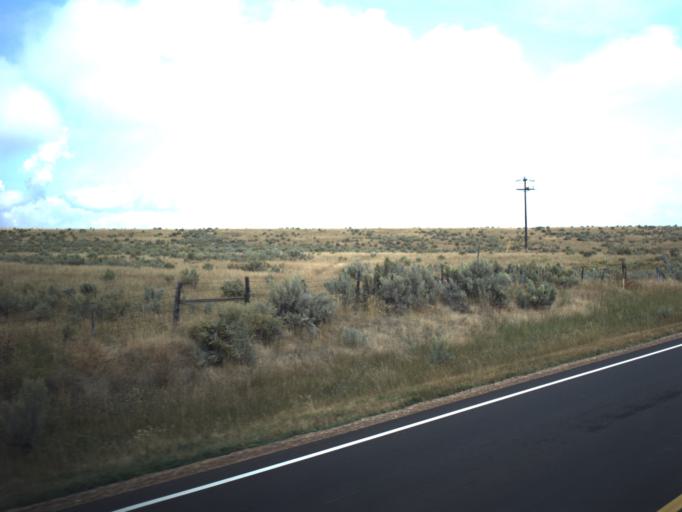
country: US
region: Utah
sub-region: Rich County
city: Randolph
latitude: 41.6872
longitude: -111.1776
